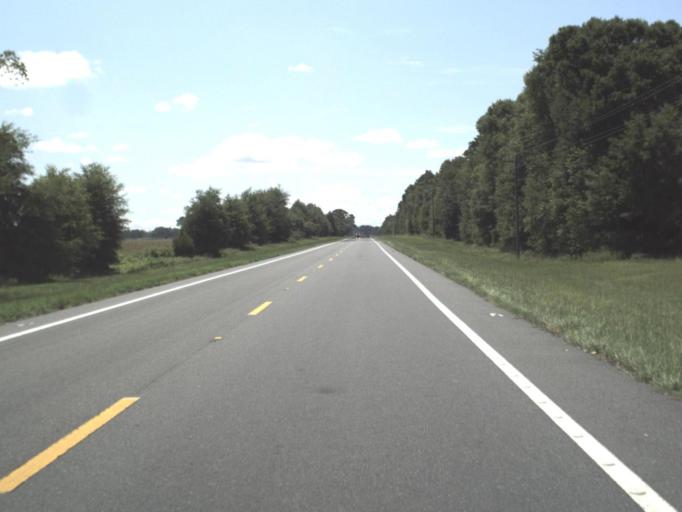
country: US
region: Florida
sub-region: Lafayette County
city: Mayo
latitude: 30.0753
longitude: -83.2086
